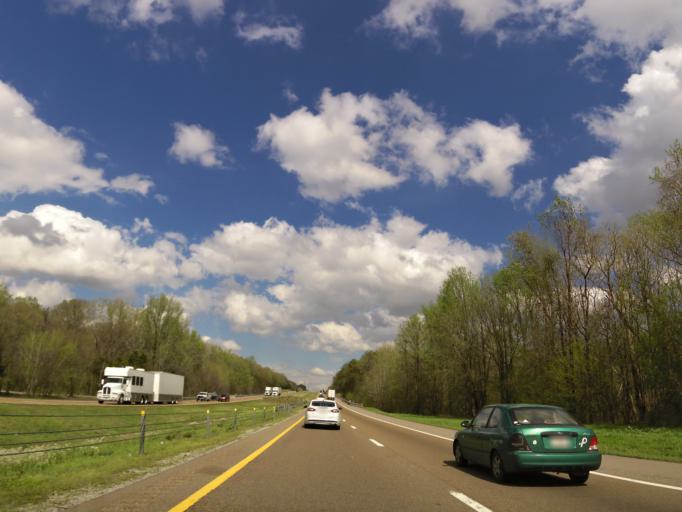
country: US
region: Tennessee
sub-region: Crockett County
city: Bells
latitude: 35.6183
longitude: -88.9959
